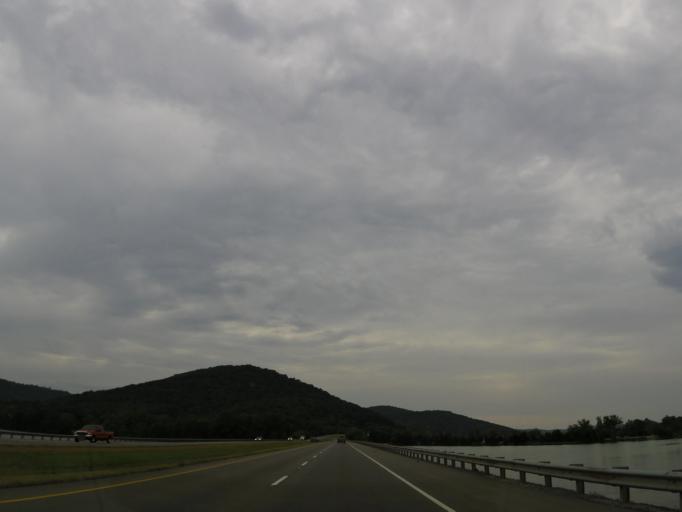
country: US
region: Alabama
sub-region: Jackson County
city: Scottsboro
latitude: 34.6191
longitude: -86.1074
